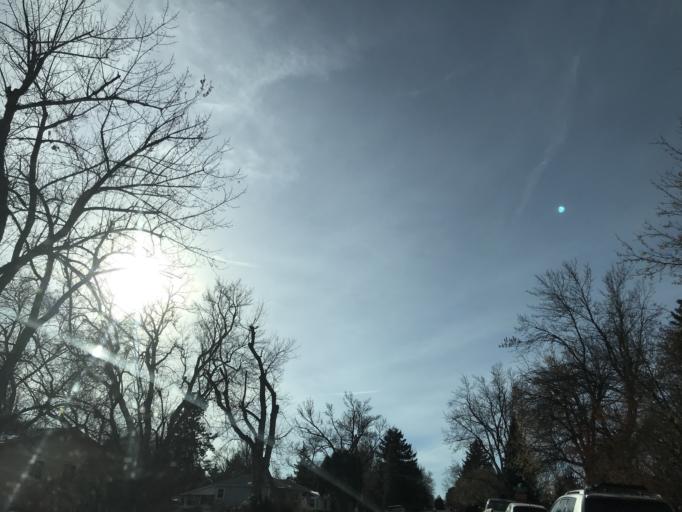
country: US
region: Colorado
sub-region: Arapahoe County
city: Littleton
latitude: 39.6029
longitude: -105.0105
